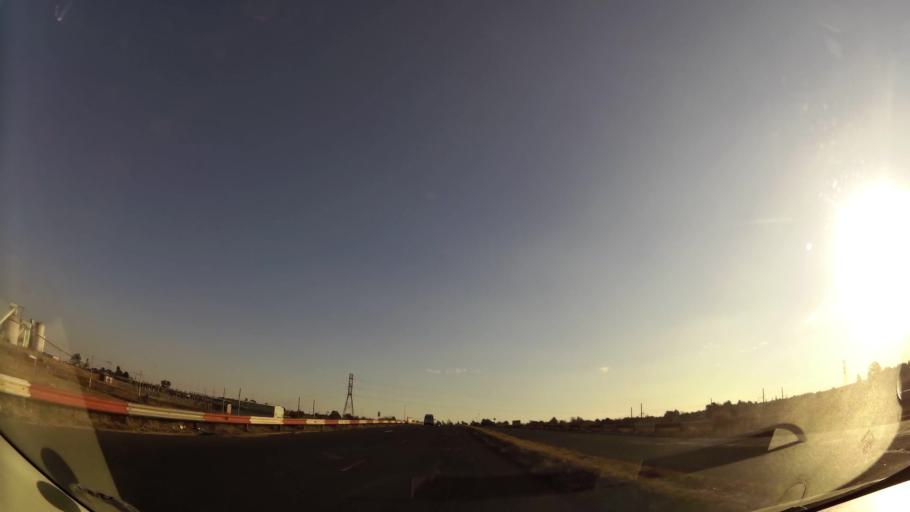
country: ZA
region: Gauteng
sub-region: West Rand District Municipality
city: Randfontein
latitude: -26.2050
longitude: 27.6640
